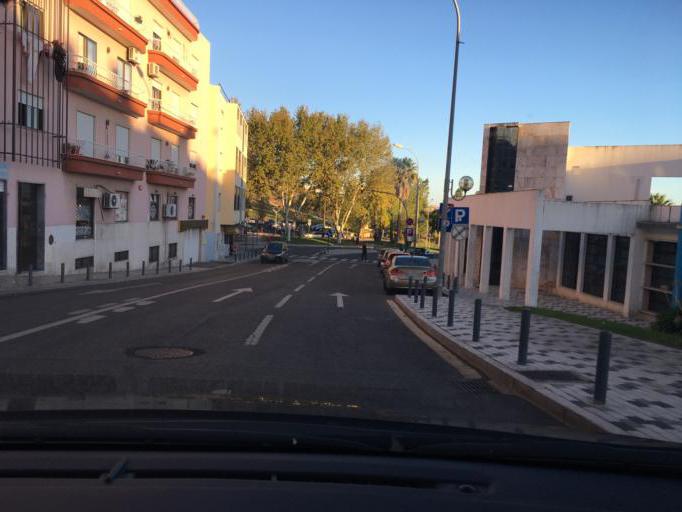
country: PT
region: Lisbon
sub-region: Odivelas
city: Pontinha
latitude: 38.7663
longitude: -9.2141
